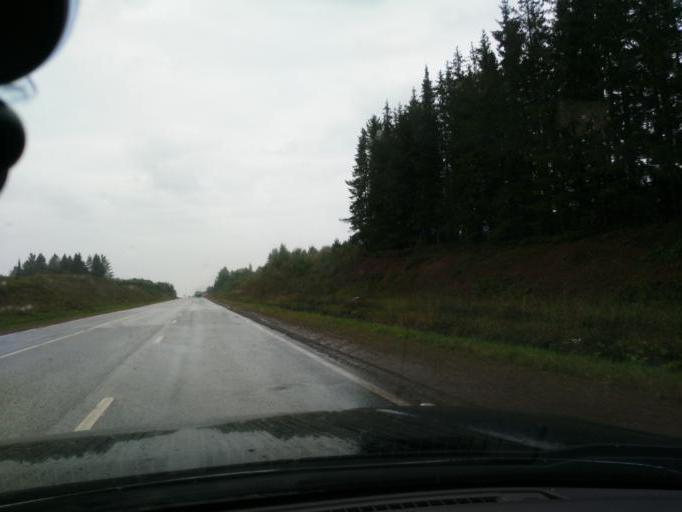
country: RU
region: Perm
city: Yugo-Kamskiy
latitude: 57.4918
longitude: 55.6849
